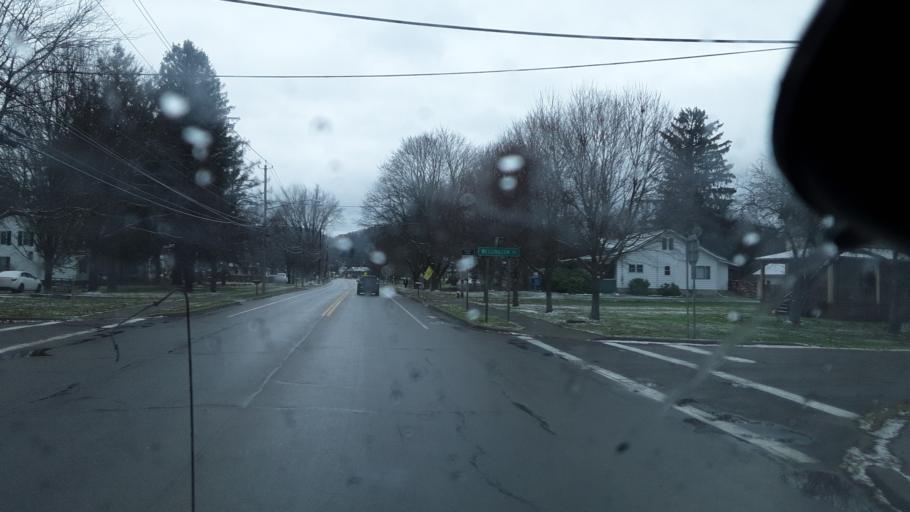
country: US
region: New York
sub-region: Cattaraugus County
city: Portville
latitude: 42.0306
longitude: -78.3379
